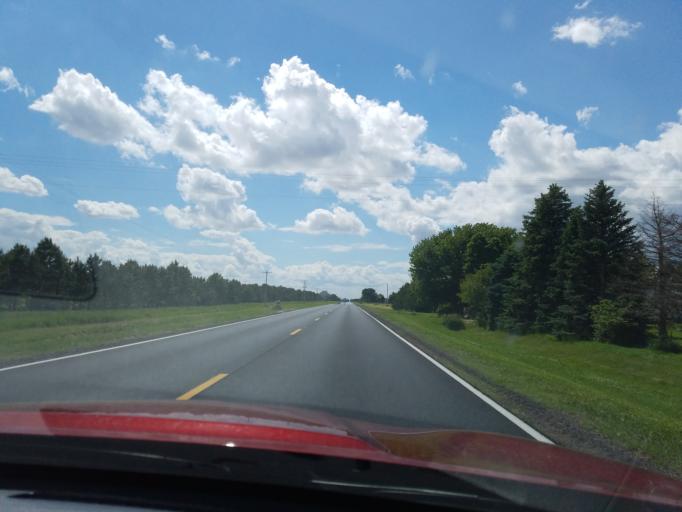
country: US
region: Nebraska
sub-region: Buffalo County
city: Kearney
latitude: 40.6410
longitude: -99.0310
